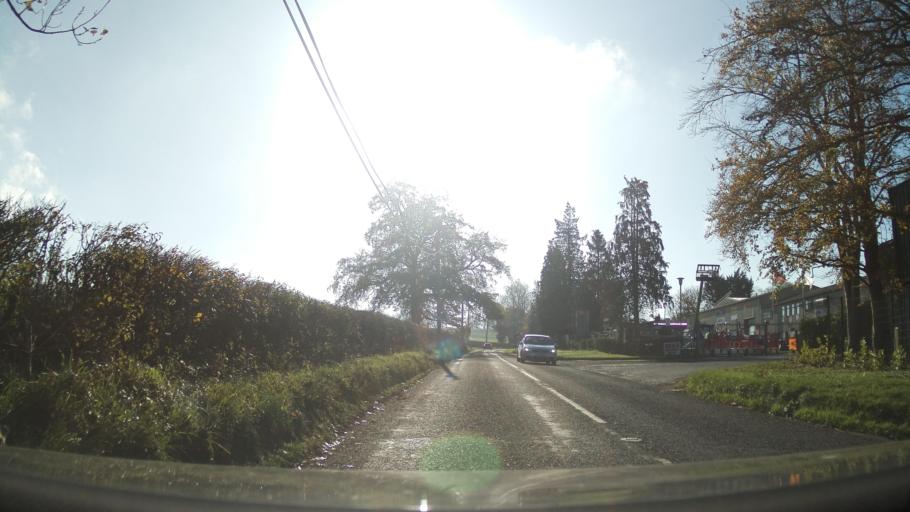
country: GB
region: England
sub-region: Somerset
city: Bruton
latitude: 51.1694
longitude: -2.4145
